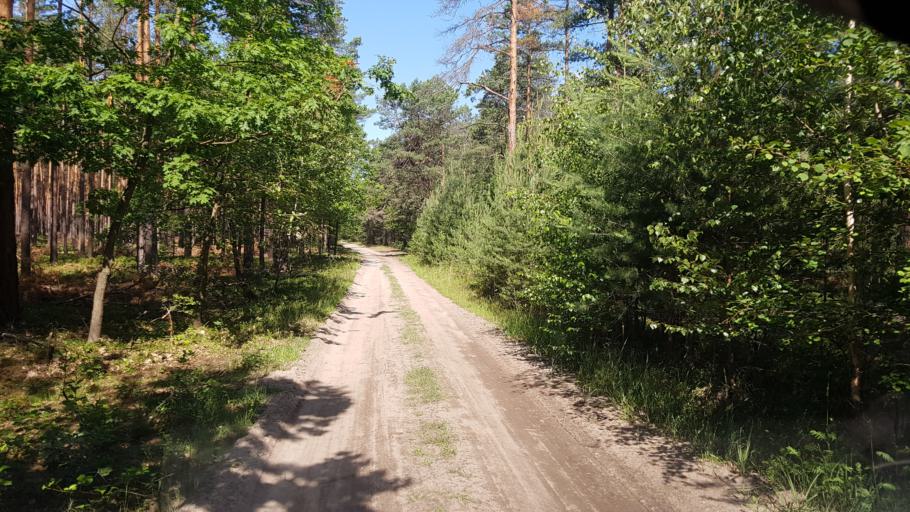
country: DE
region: Brandenburg
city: Sallgast
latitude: 51.6024
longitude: 13.8068
